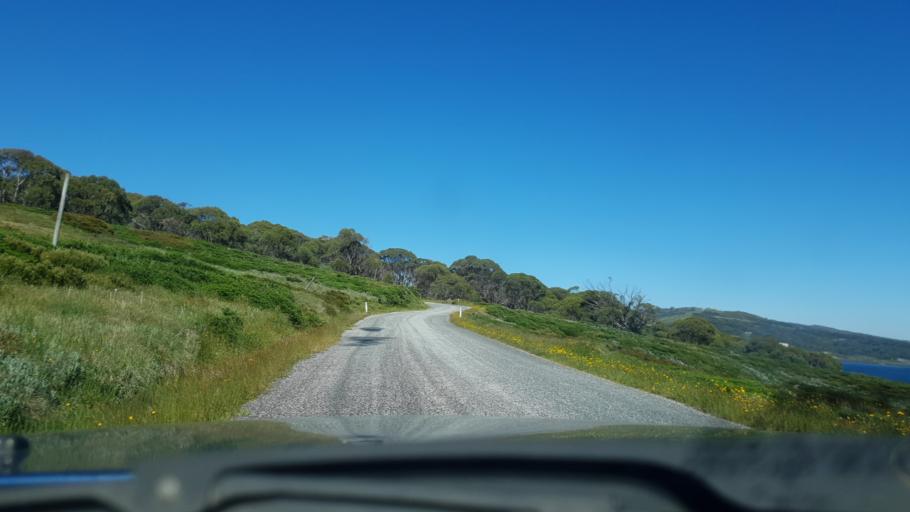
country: AU
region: Victoria
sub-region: Alpine
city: Mount Beauty
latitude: -36.8832
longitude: 147.3106
